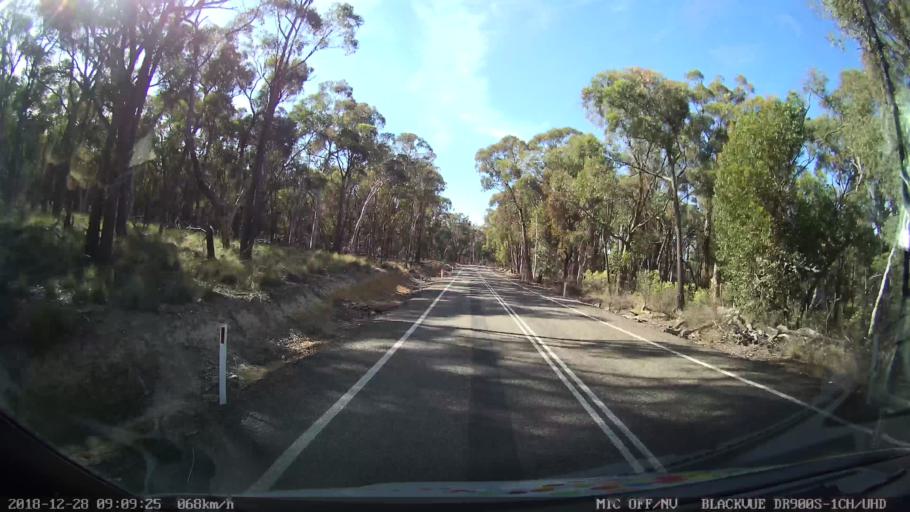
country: AU
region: New South Wales
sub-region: Upper Lachlan Shire
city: Crookwell
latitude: -34.2213
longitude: 149.3356
